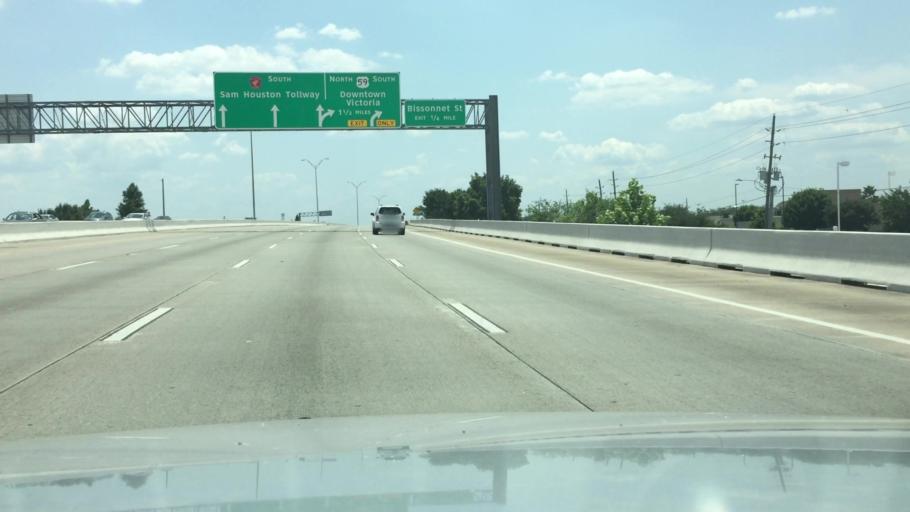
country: US
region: Texas
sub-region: Fort Bend County
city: Meadows Place
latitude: 29.6920
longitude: -95.5573
